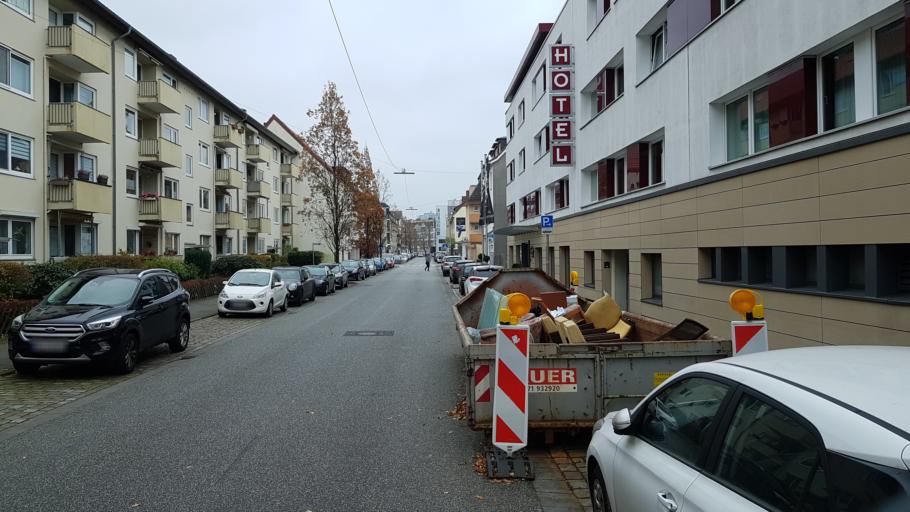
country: DE
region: Bremen
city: Bremerhaven
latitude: 53.5439
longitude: 8.5810
